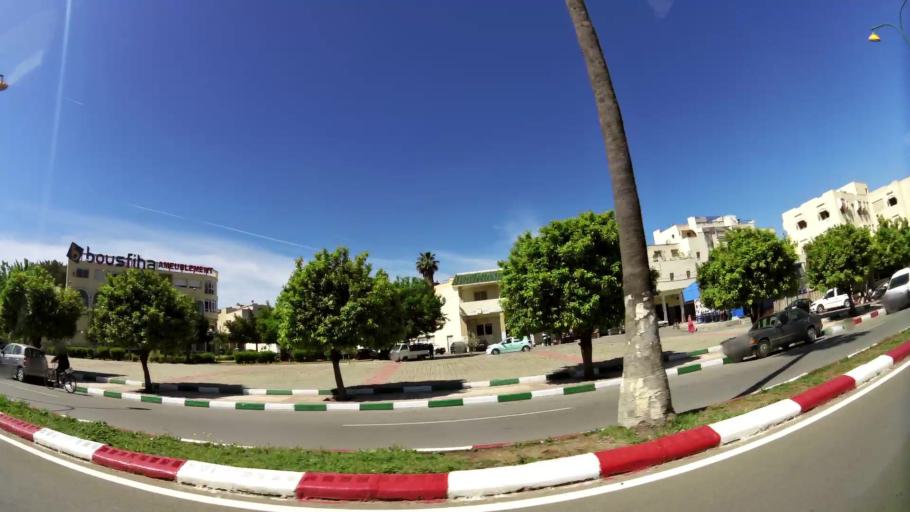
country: MA
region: Meknes-Tafilalet
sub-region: Meknes
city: Meknes
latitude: 33.8932
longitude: -5.5554
